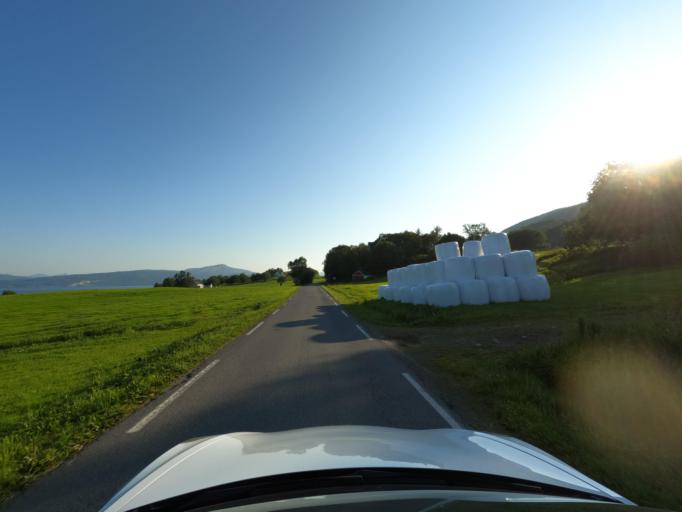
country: NO
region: Nordland
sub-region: Evenes
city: Randa
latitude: 68.4739
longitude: 16.8787
